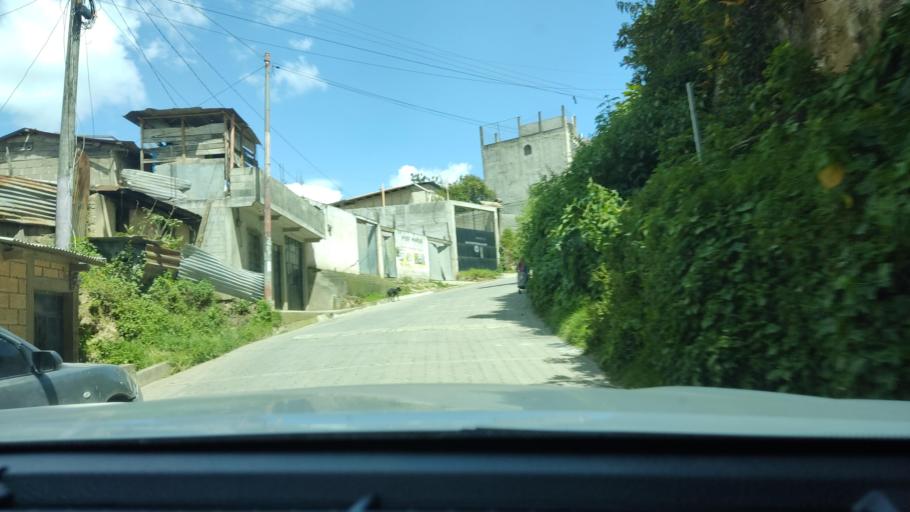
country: GT
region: Chimaltenango
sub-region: Municipio de San Juan Comalapa
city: Comalapa
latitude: 14.7445
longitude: -90.8879
